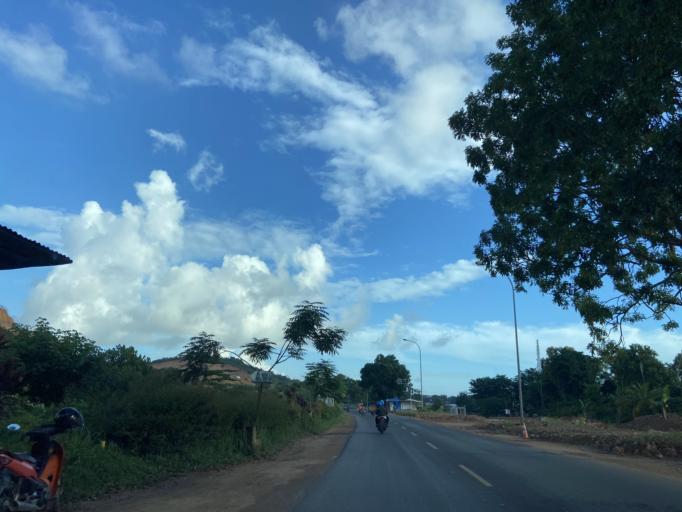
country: SG
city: Singapore
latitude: 1.0257
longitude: 104.0090
